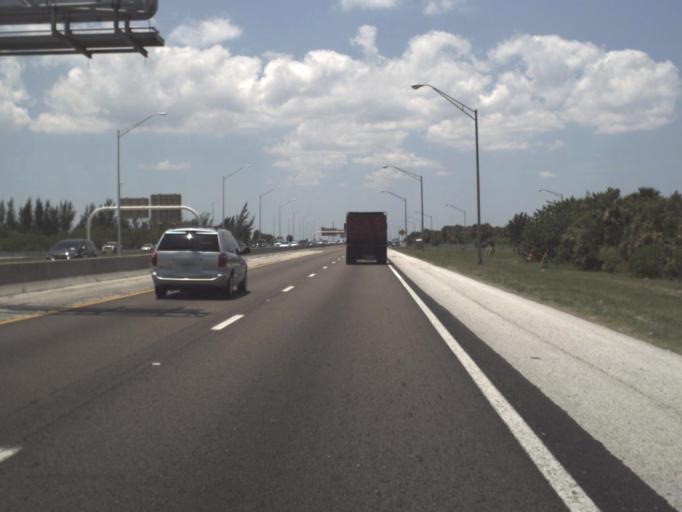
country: US
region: Florida
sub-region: Hillsborough County
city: Town 'n' Country
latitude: 27.9442
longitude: -82.5414
